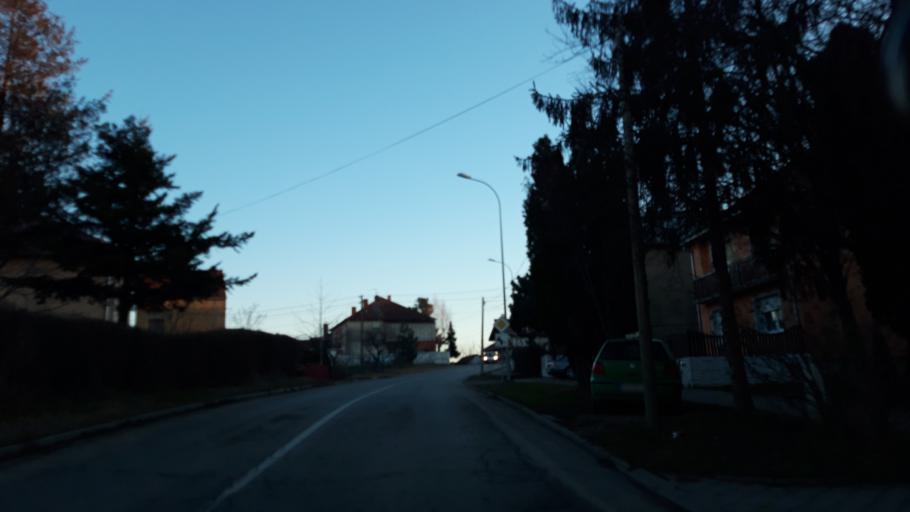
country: RS
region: Autonomna Pokrajina Vojvodina
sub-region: Sremski Okrug
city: Ingija
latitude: 45.0507
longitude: 20.0679
